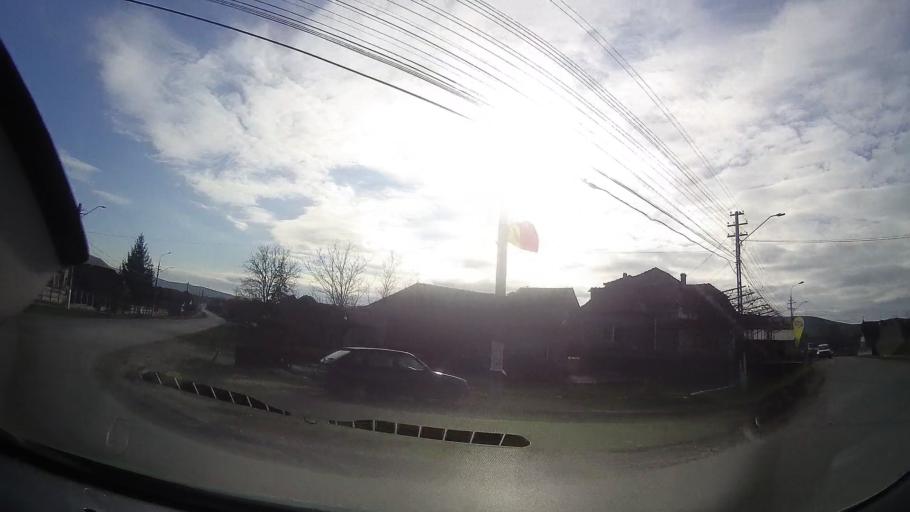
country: RO
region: Mures
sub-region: Comuna Valea Larga
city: Valea Larga
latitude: 46.6213
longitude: 24.0768
